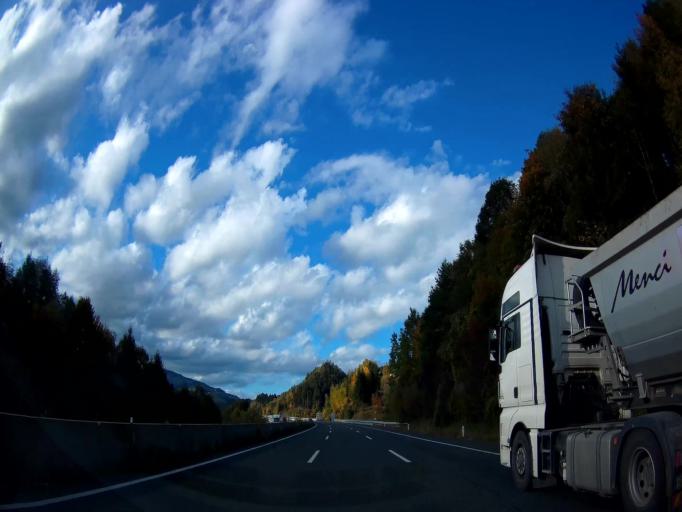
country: AT
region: Carinthia
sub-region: Politischer Bezirk Wolfsberg
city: Wolfsberg
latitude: 46.8827
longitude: 14.8299
